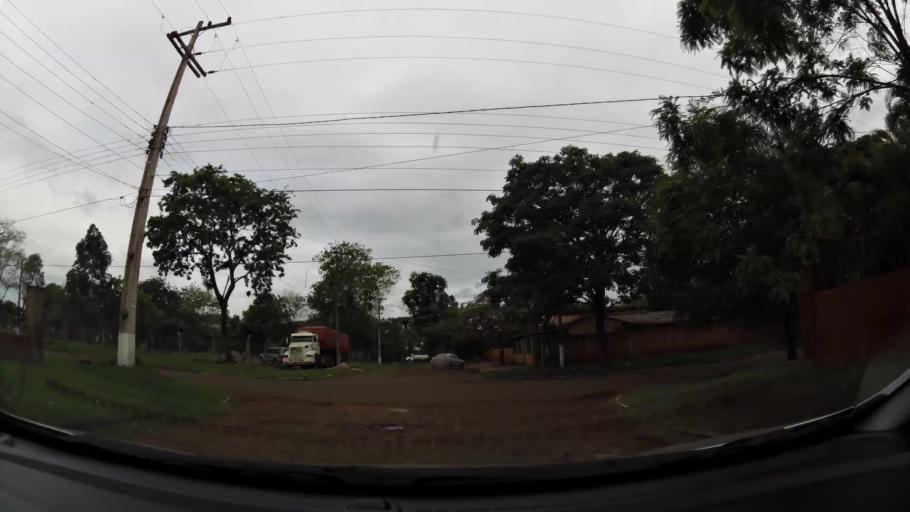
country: PY
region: Alto Parana
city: Ciudad del Este
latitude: -25.4087
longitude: -54.6332
